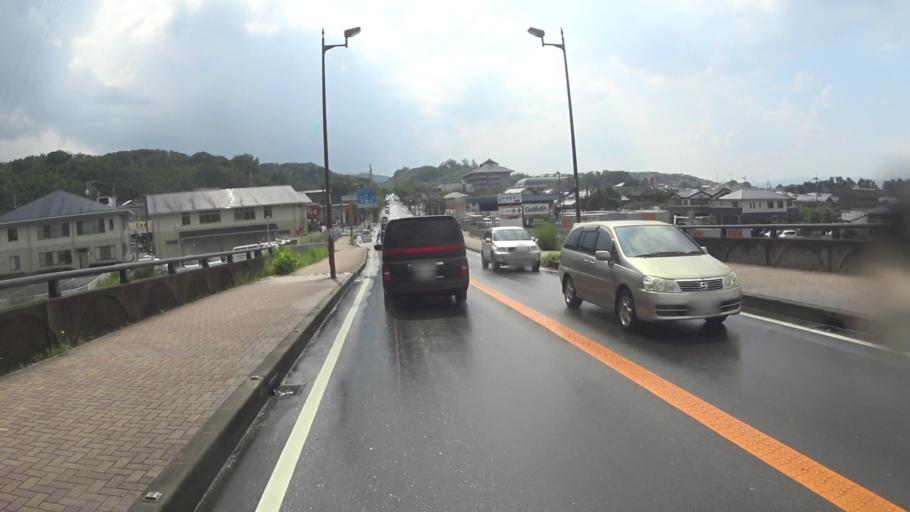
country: JP
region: Kyoto
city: Tanabe
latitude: 34.8139
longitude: 135.7727
